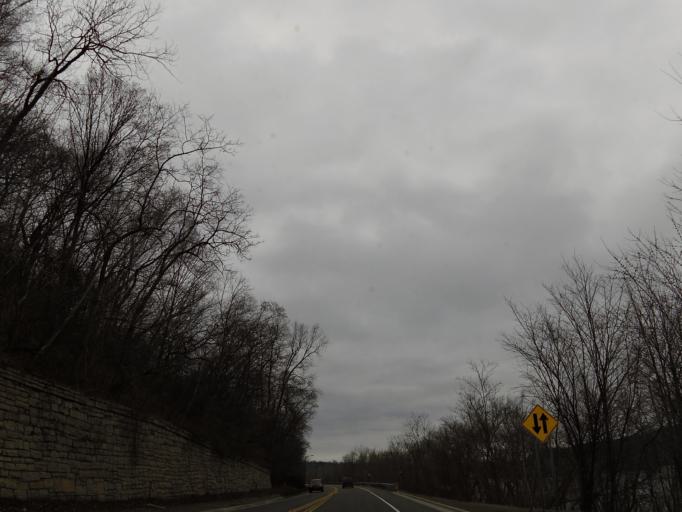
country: US
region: Minnesota
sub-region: Washington County
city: Stillwater
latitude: 45.0456
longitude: -92.7966
